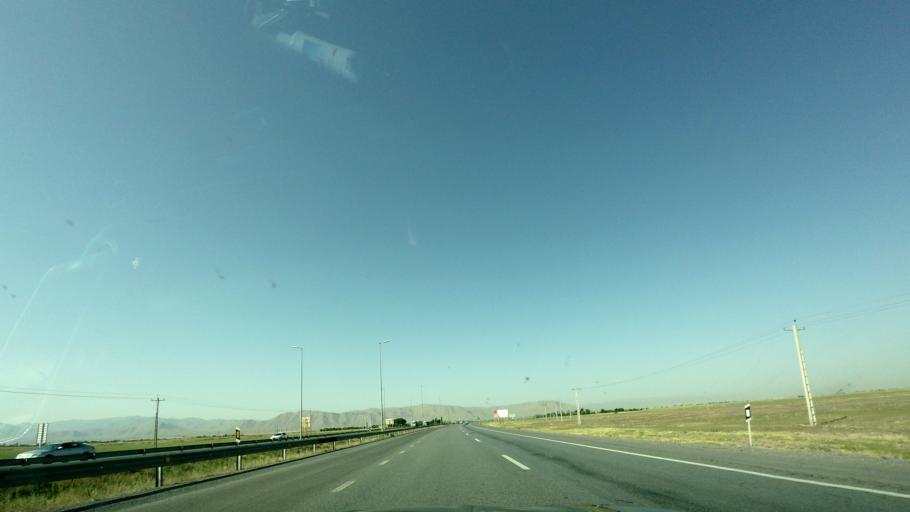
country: IR
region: Markazi
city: Ashtian
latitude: 34.1896
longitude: 50.0534
